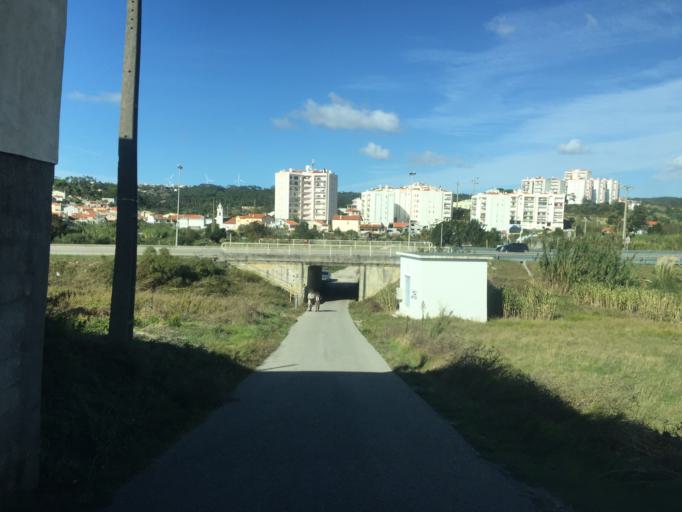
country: PT
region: Coimbra
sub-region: Figueira da Foz
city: Tavarede
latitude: 40.1631
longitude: -8.8433
